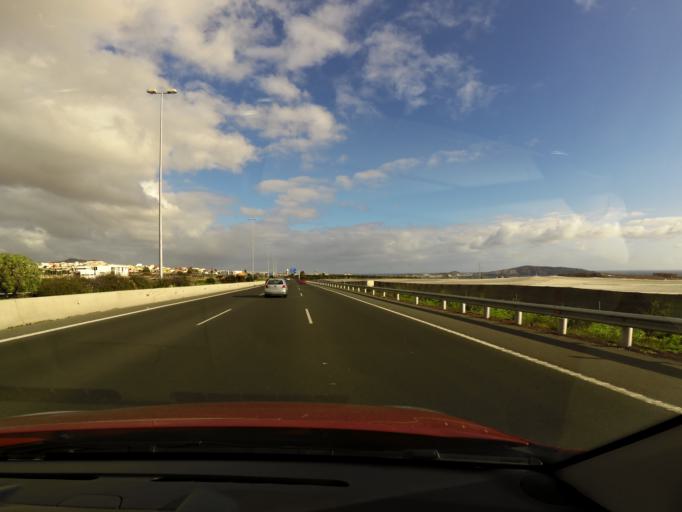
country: ES
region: Canary Islands
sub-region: Provincia de Las Palmas
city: Ingenio
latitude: 27.9096
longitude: -15.3994
